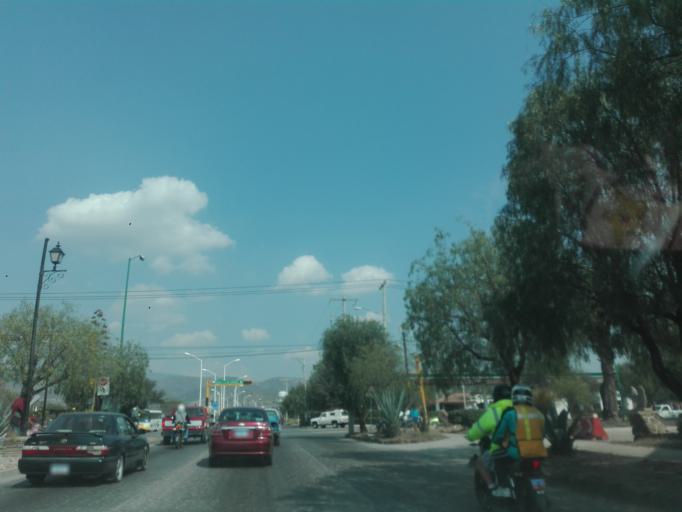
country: MX
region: Guanajuato
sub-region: Leon
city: Fraccionamiento Paraiso Real
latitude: 21.1130
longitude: -101.6058
